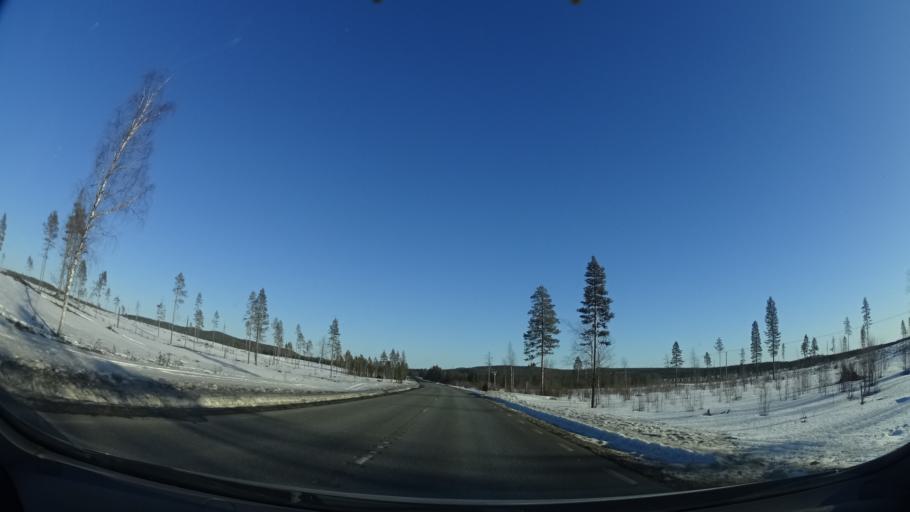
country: SE
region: Vaesterbotten
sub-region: Skelleftea Kommun
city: Langsele
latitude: 65.0383
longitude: 20.0879
